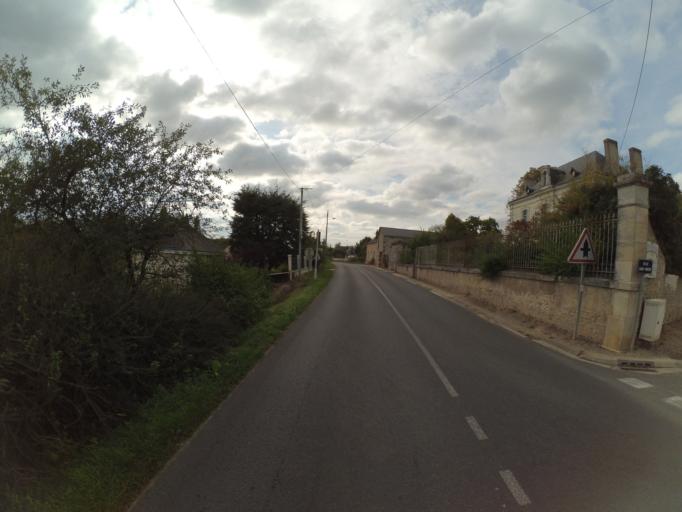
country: FR
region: Centre
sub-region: Departement d'Indre-et-Loire
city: Noizay
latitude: 47.4497
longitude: 0.8704
